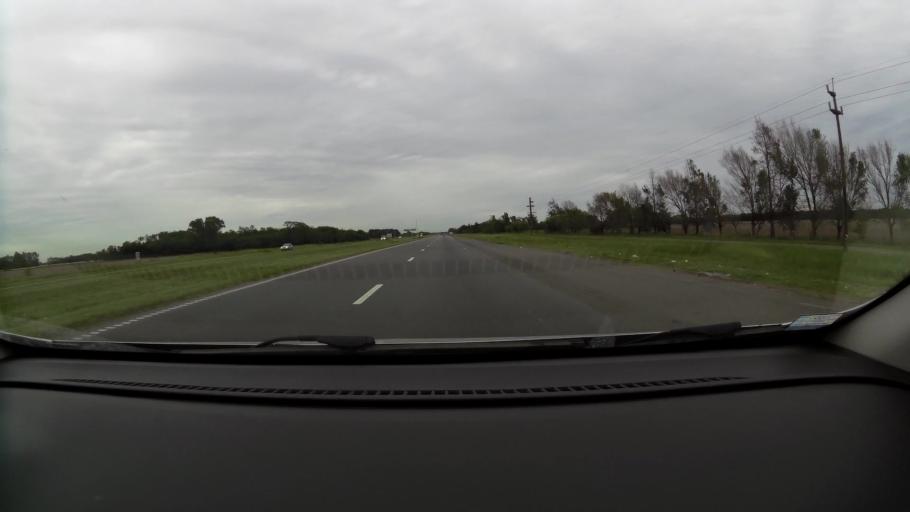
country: AR
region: Buenos Aires
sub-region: Partido de Zarate
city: Zarate
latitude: -34.0789
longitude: -59.2139
